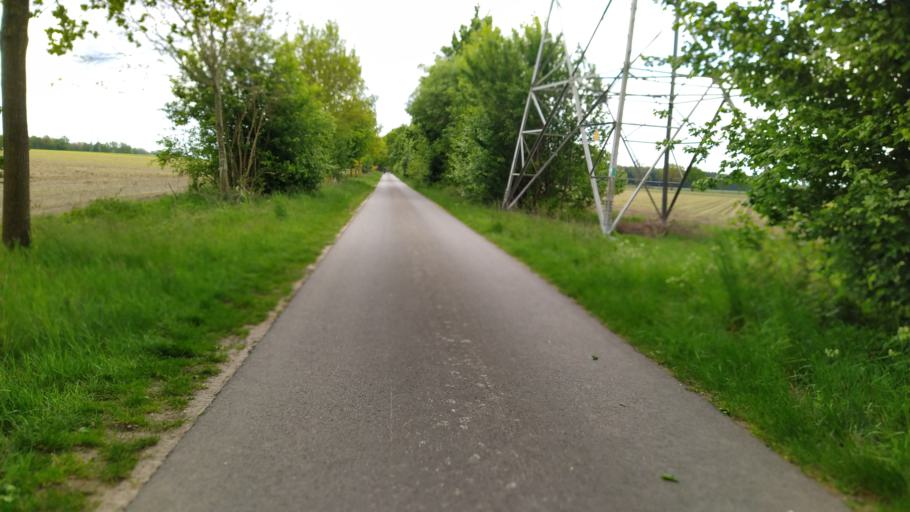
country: DE
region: Lower Saxony
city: Ahlerstedt
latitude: 53.3736
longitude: 9.3960
